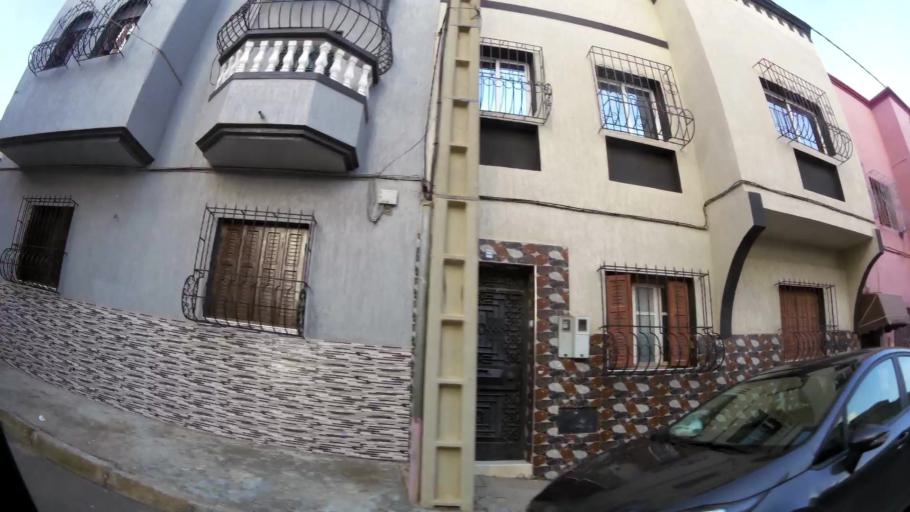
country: MA
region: Chaouia-Ouardigha
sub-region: Settat Province
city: Settat
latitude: 33.0038
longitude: -7.6380
